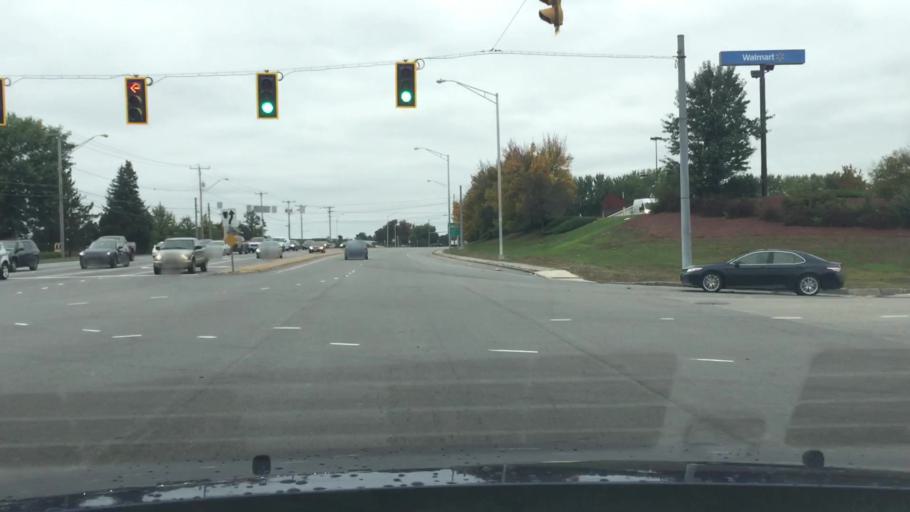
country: US
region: New Hampshire
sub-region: Hillsborough County
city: Hudson
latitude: 42.7259
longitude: -71.4238
